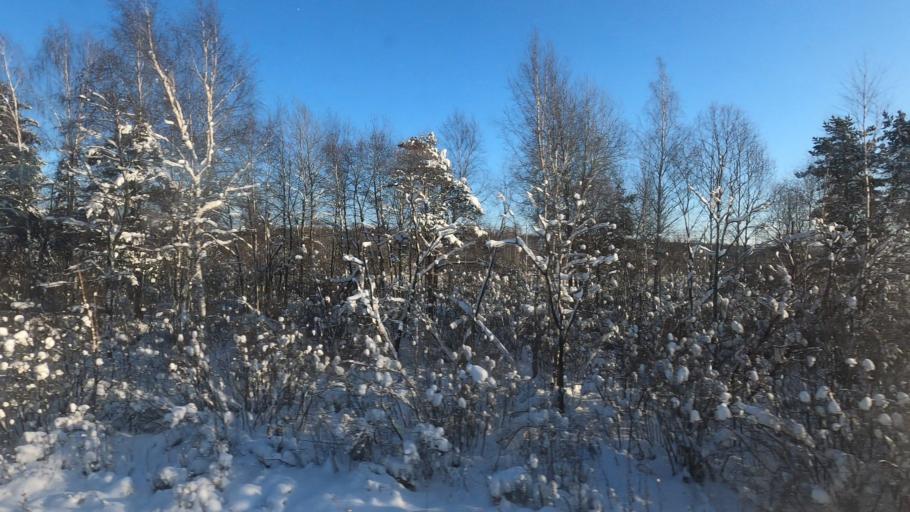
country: RU
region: Moskovskaya
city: Orud'yevo
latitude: 56.4526
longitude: 37.5261
